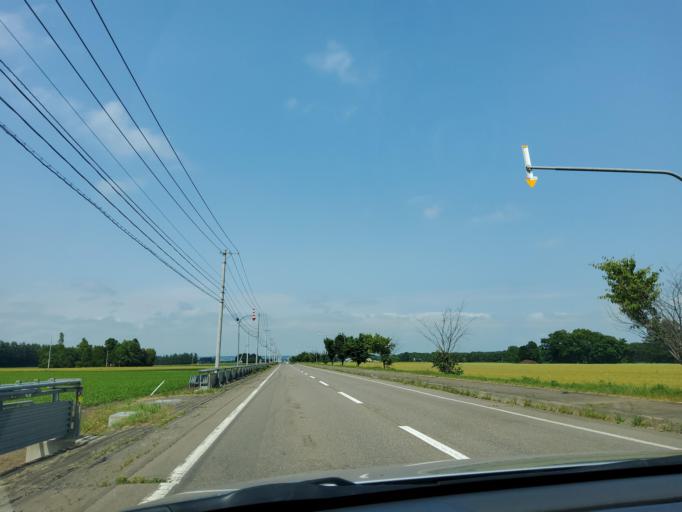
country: JP
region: Hokkaido
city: Obihiro
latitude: 42.8816
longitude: 143.0326
